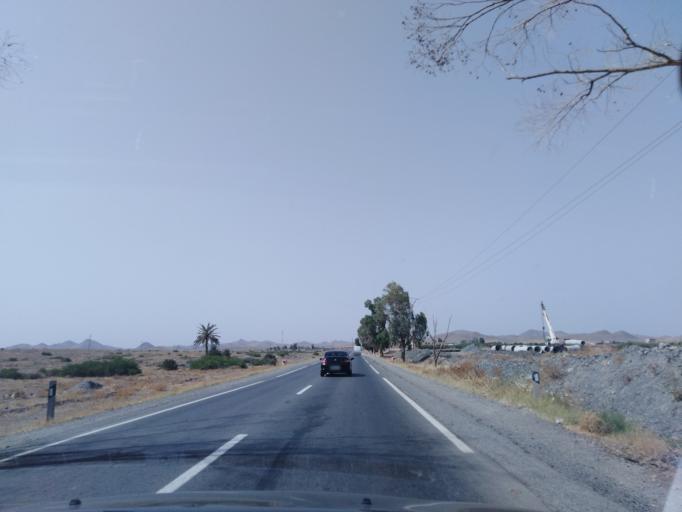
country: MA
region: Marrakech-Tensift-Al Haouz
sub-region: Kelaa-Des-Sraghna
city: Sidi Bou Othmane
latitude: 31.7789
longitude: -7.9783
